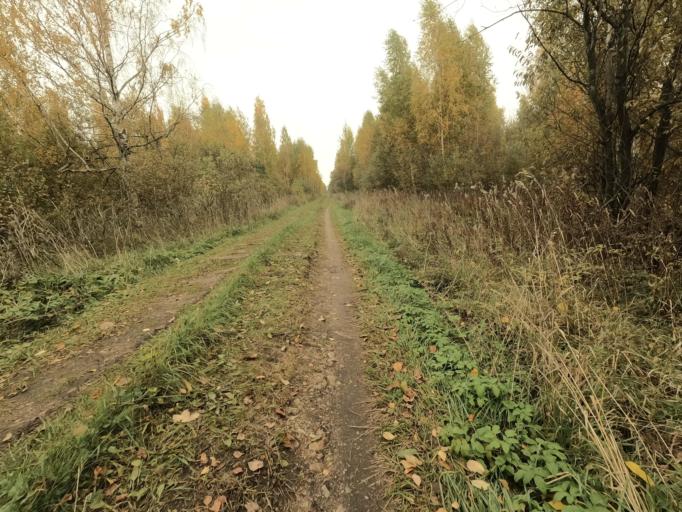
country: RU
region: Novgorod
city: Pankovka
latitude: 58.8826
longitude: 30.9444
